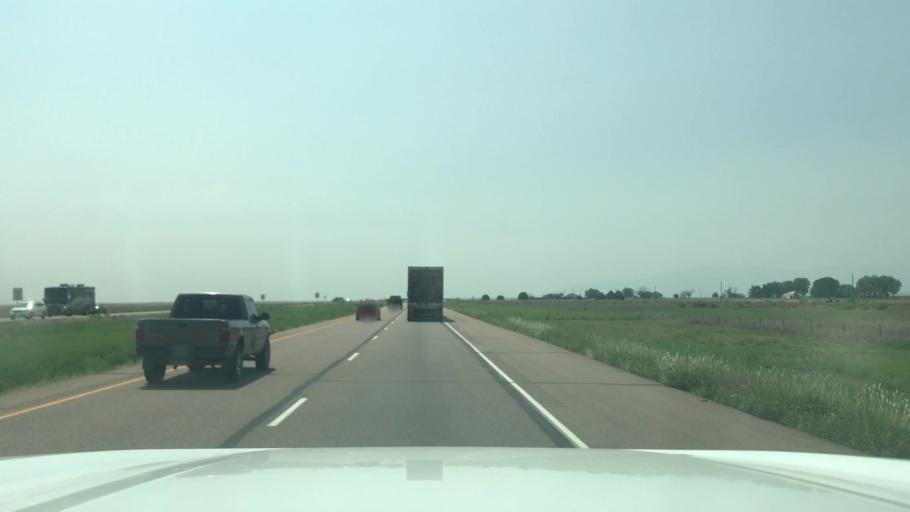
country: US
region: Colorado
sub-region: Pueblo County
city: Pueblo
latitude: 38.1699
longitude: -104.6374
